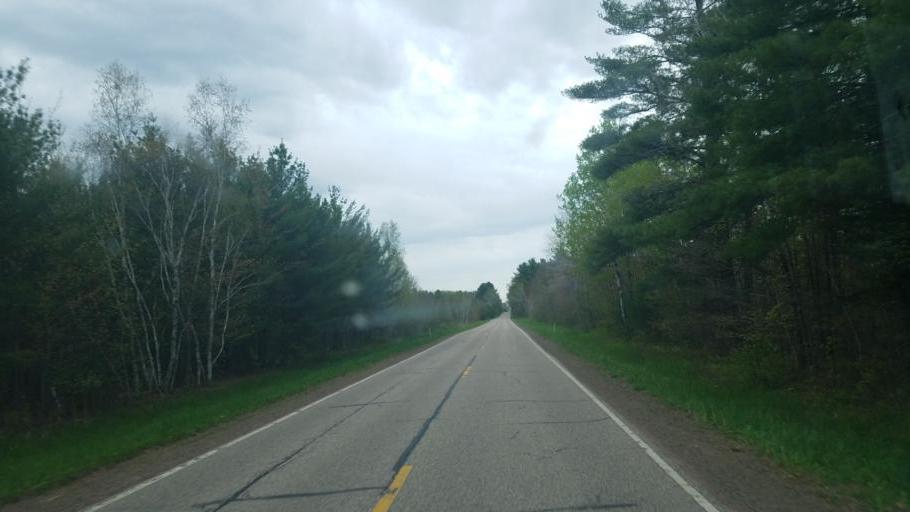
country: US
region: Wisconsin
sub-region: Wood County
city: Marshfield
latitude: 44.5320
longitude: -90.2996
